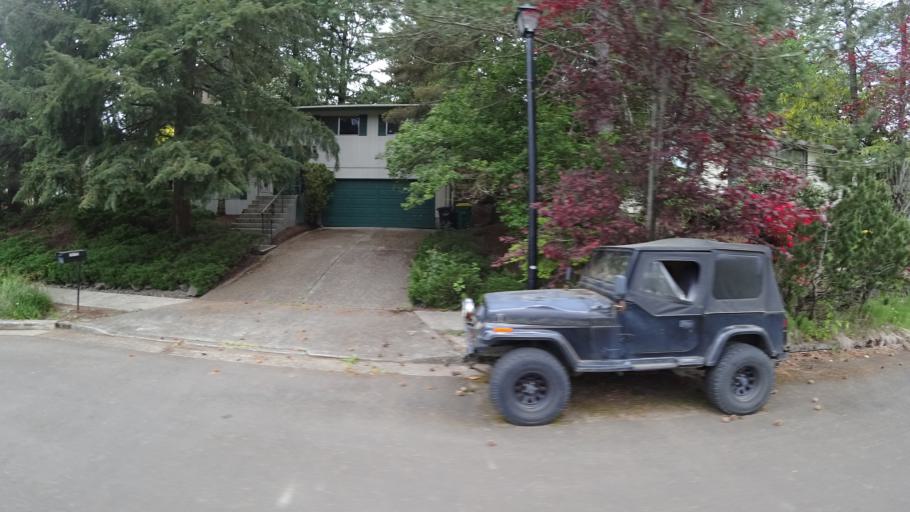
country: US
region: Oregon
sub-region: Washington County
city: Beaverton
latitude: 45.4788
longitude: -122.8311
